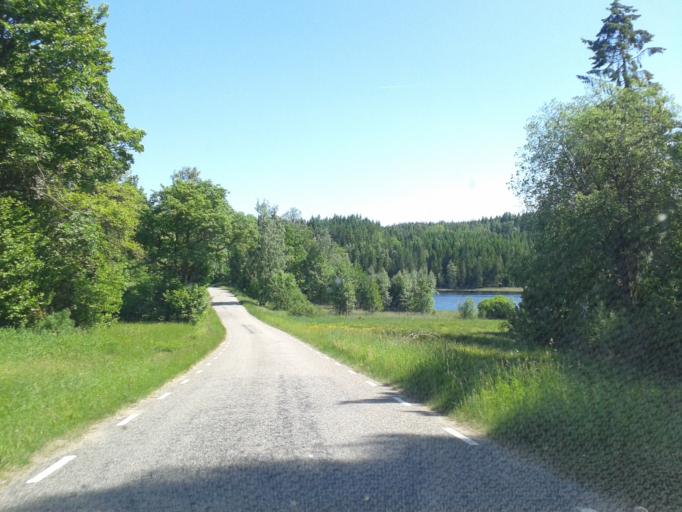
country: SE
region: Vaestra Goetaland
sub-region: Stenungsunds Kommun
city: Stora Hoga
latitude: 57.9988
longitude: 11.9338
